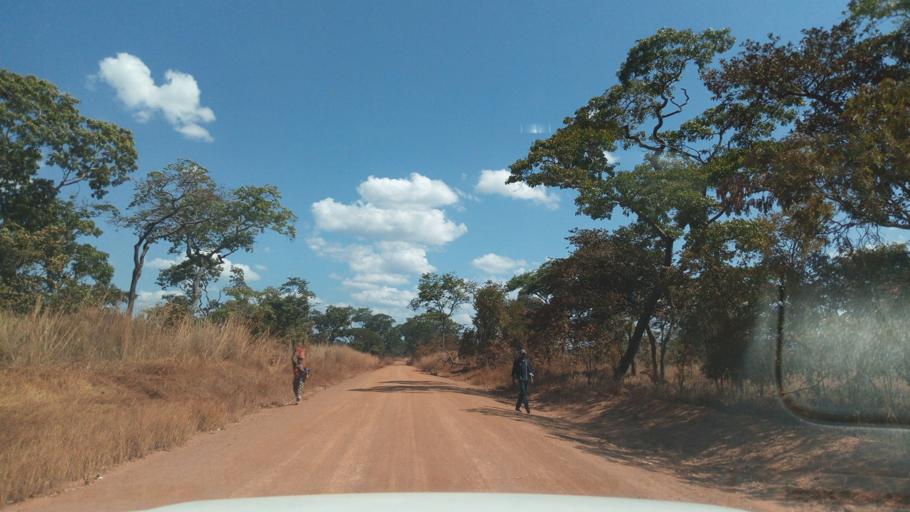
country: ZM
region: Luapula
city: Mwense
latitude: -10.7226
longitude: 28.2113
